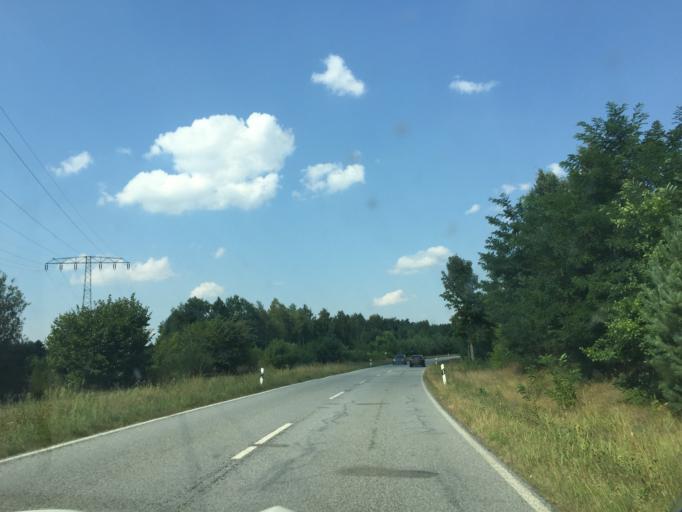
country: DE
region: Saxony
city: Boxberg
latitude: 51.4297
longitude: 14.5284
